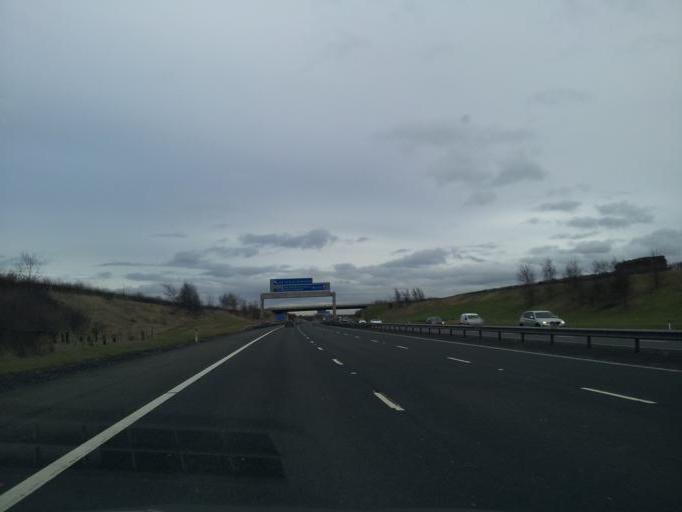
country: GB
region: England
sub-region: Staffordshire
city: Shenstone
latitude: 52.6464
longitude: -1.8297
